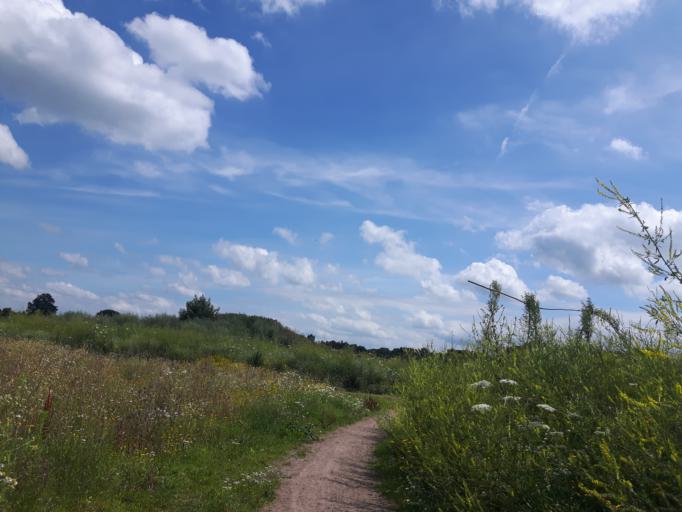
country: NL
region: Overijssel
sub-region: Gemeente Haaksbergen
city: Haaksbergen
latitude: 52.1712
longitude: 6.7510
